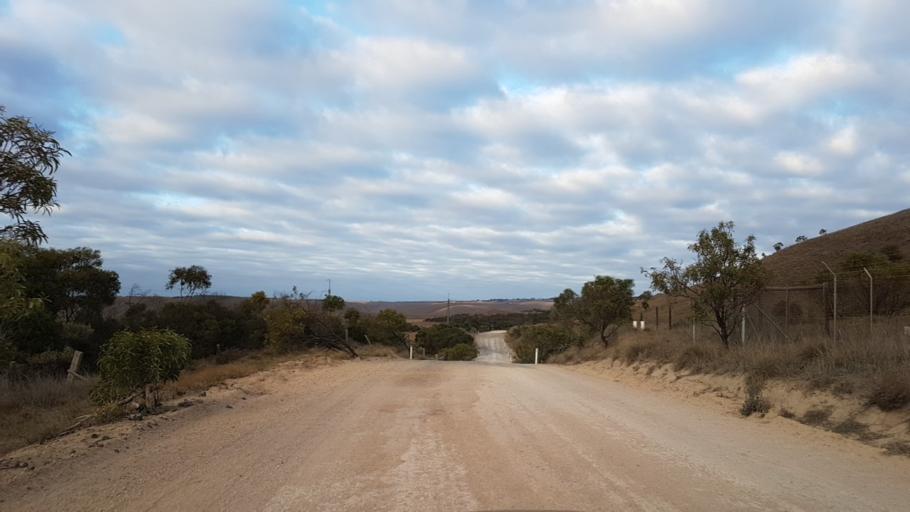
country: AU
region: South Australia
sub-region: Mount Barker
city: Callington
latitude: -35.0976
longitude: 139.0074
